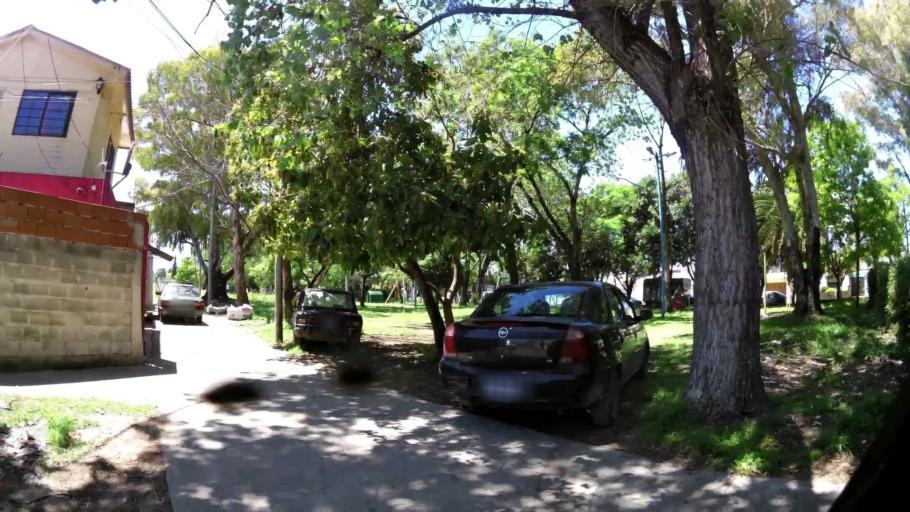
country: AR
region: Buenos Aires
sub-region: Partido de Quilmes
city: Quilmes
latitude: -34.7140
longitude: -58.3141
